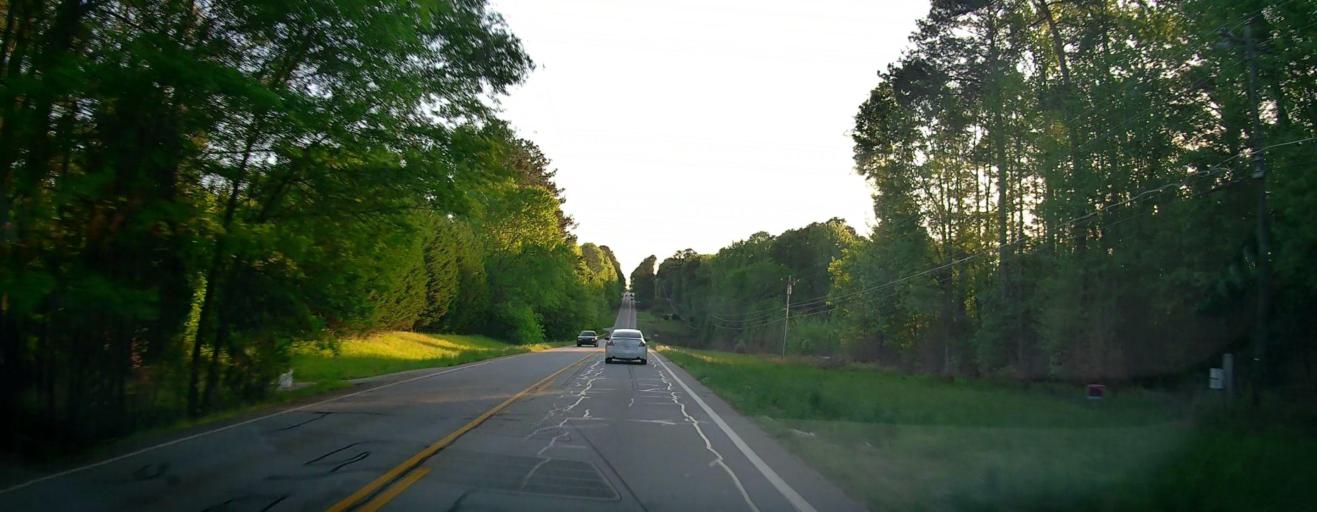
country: US
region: Georgia
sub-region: Newton County
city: Oakwood
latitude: 33.5526
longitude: -83.9325
